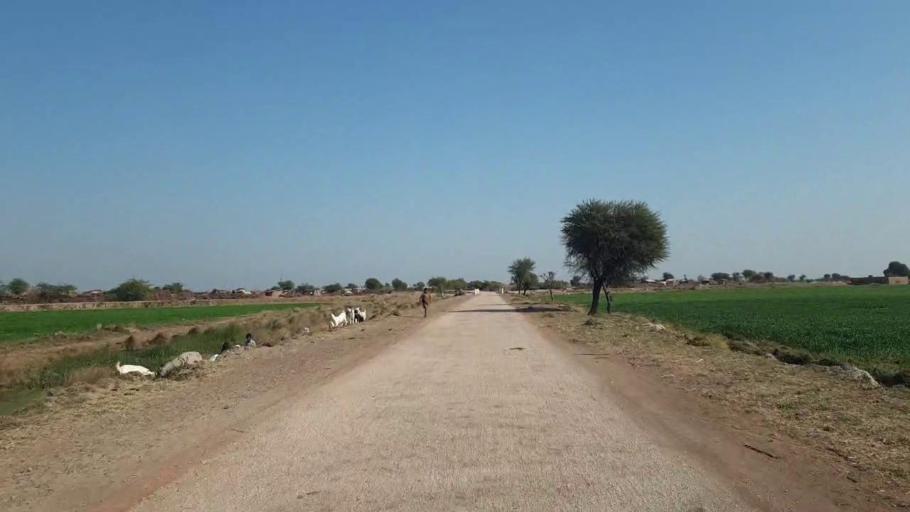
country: PK
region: Sindh
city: Shahdadpur
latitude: 25.9792
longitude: 68.6609
